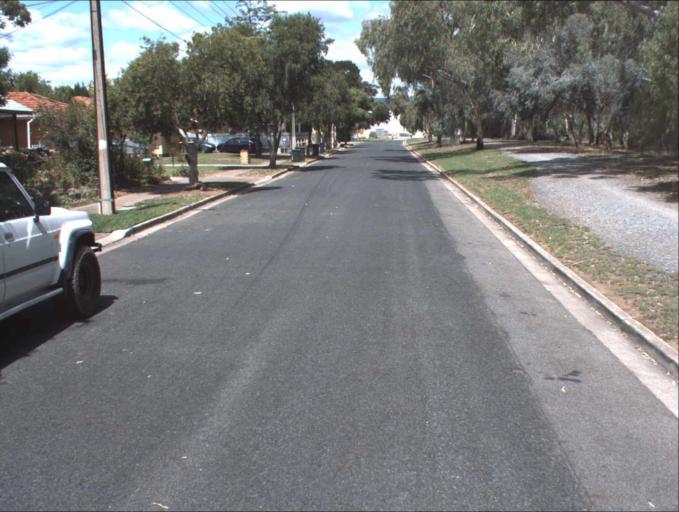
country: AU
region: South Australia
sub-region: Port Adelaide Enfield
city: Gilles Plains
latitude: -34.8433
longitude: 138.6600
